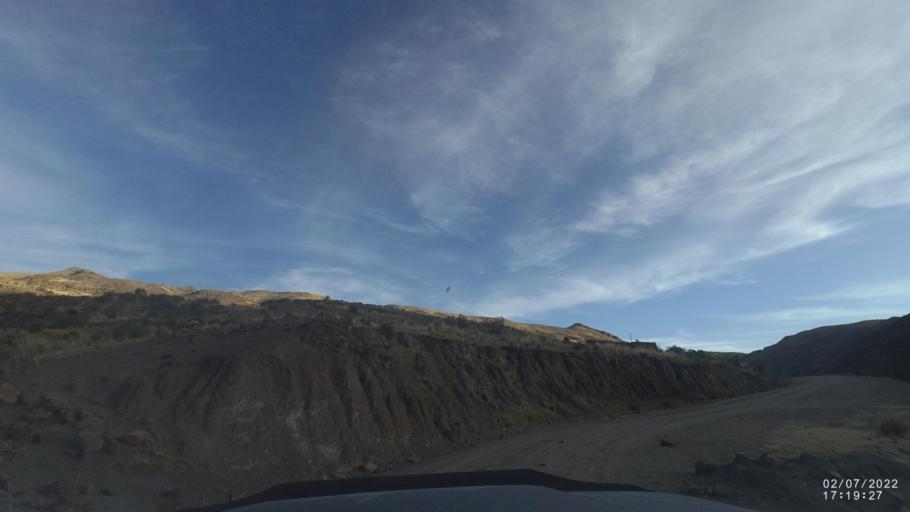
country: BO
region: Cochabamba
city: Irpa Irpa
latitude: -17.8743
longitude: -66.5908
